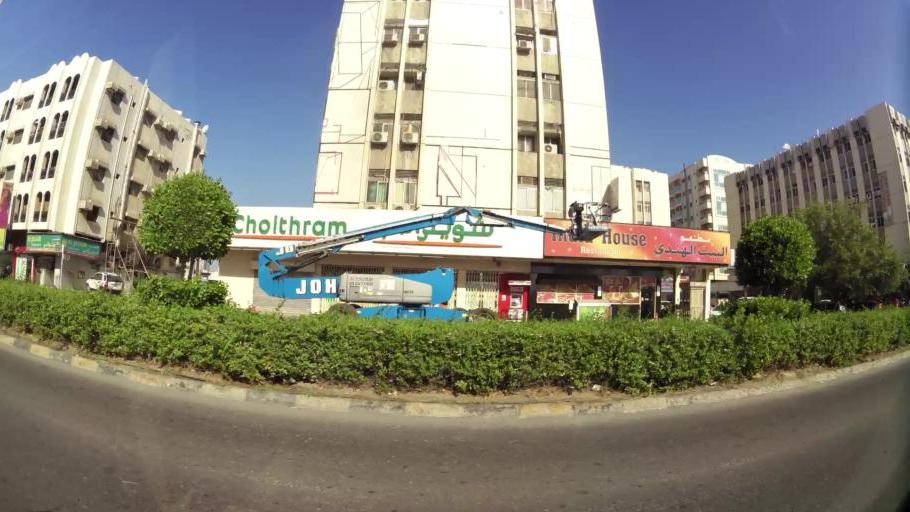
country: AE
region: Ajman
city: Ajman
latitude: 25.4102
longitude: 55.4437
